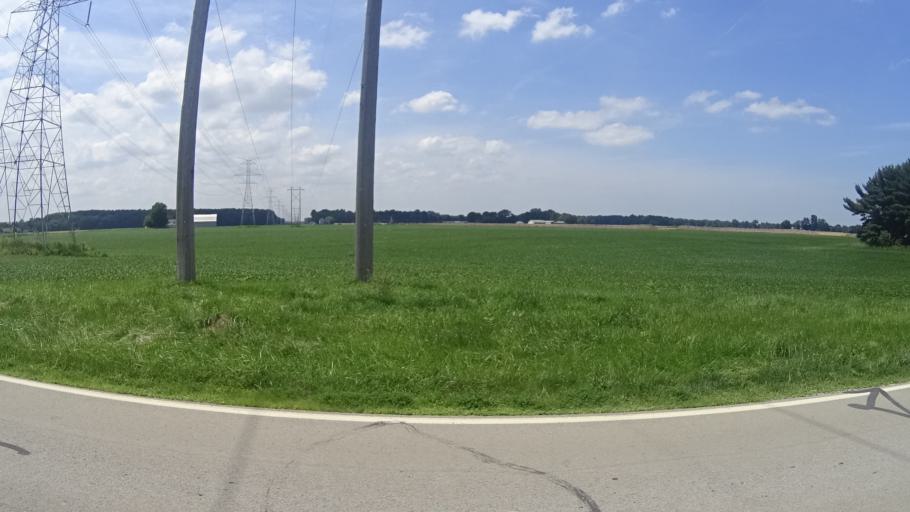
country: US
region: Ohio
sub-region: Erie County
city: Huron
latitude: 41.3358
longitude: -82.5363
